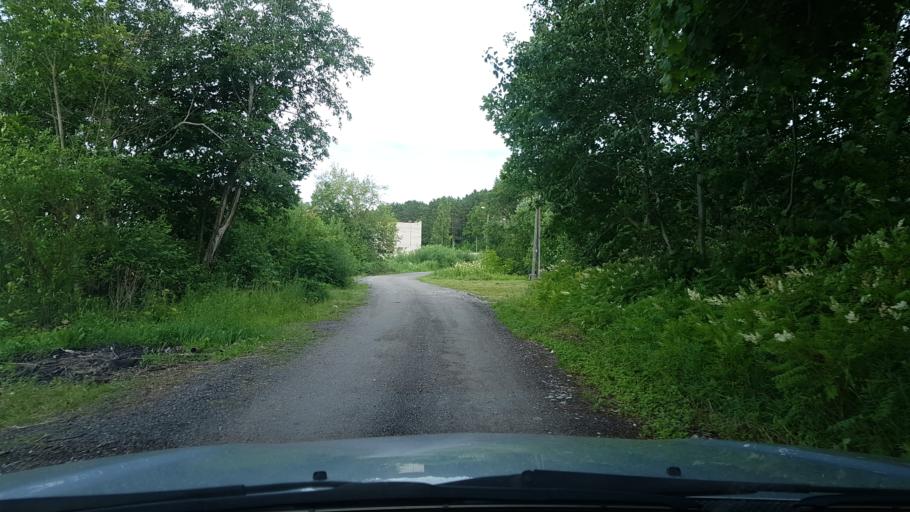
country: EE
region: Ida-Virumaa
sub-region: Narva-Joesuu linn
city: Narva-Joesuu
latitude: 59.4605
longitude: 28.0530
